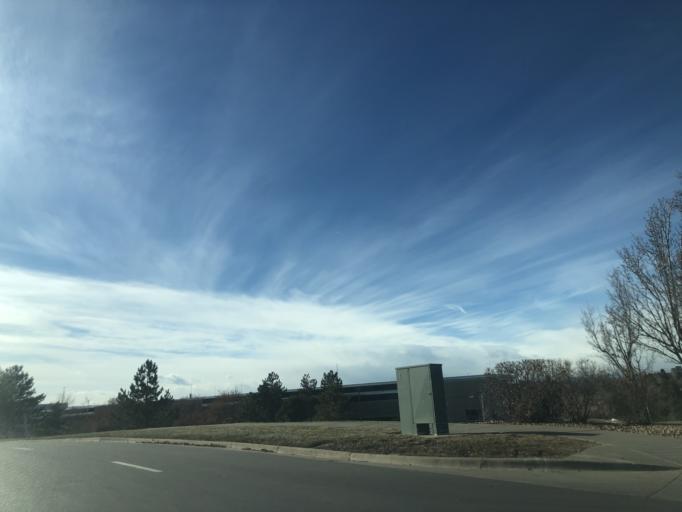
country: US
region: Colorado
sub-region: Douglas County
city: Meridian
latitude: 39.5614
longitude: -104.8586
